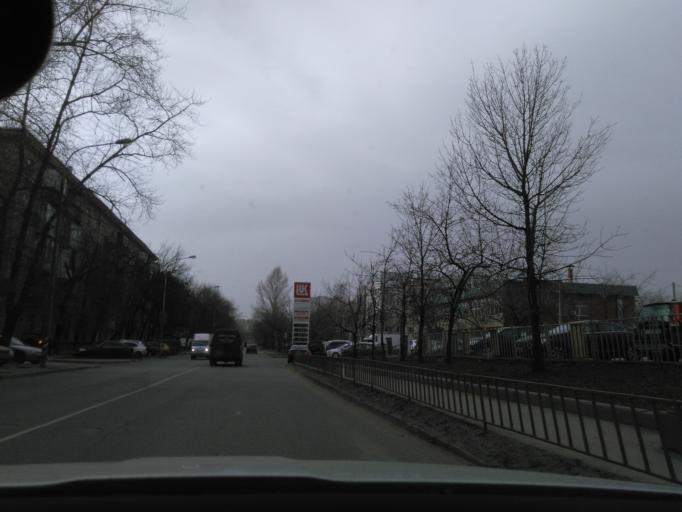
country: RU
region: Moskovskaya
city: Koptevo
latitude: 55.8318
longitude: 37.5193
